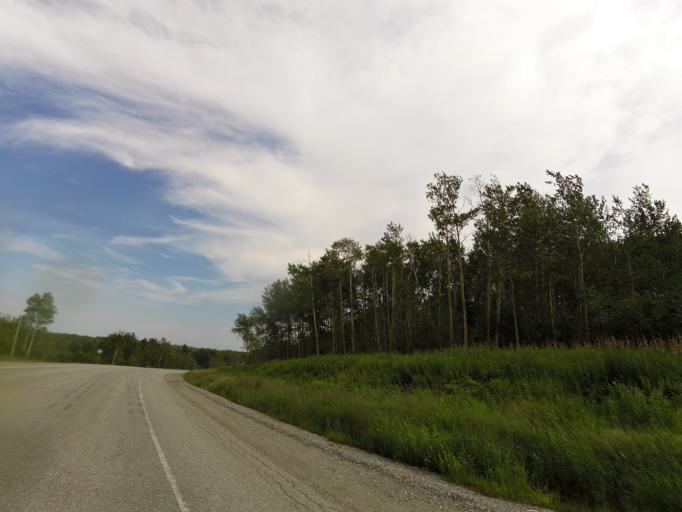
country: CA
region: Quebec
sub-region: Abitibi-Temiscamingue
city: Malartic
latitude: 48.2334
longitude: -78.4122
